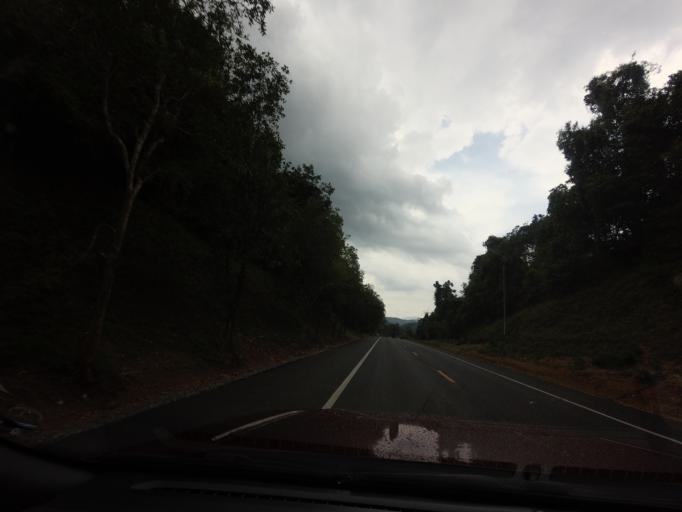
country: TH
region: Yala
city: Ban Nang Sata
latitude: 6.2301
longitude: 101.2187
